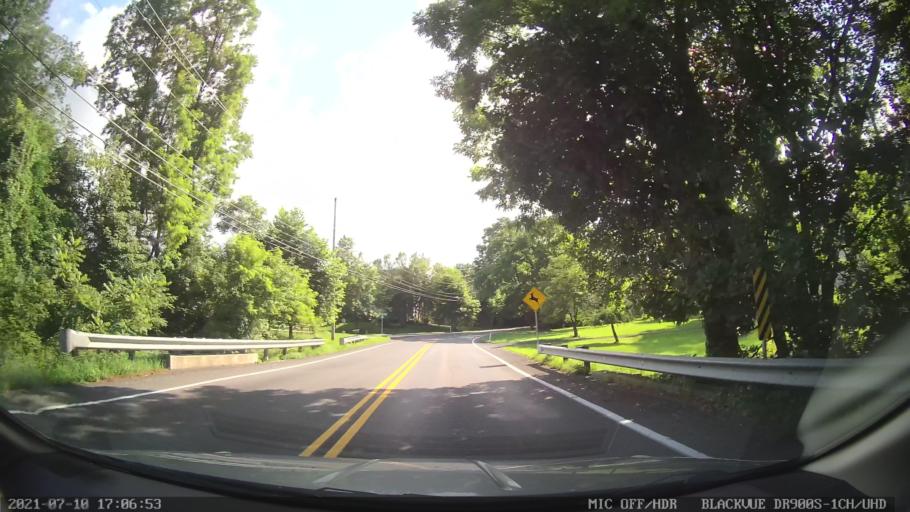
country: US
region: Pennsylvania
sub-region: Lehigh County
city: Coopersburg
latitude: 40.5236
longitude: -75.3931
